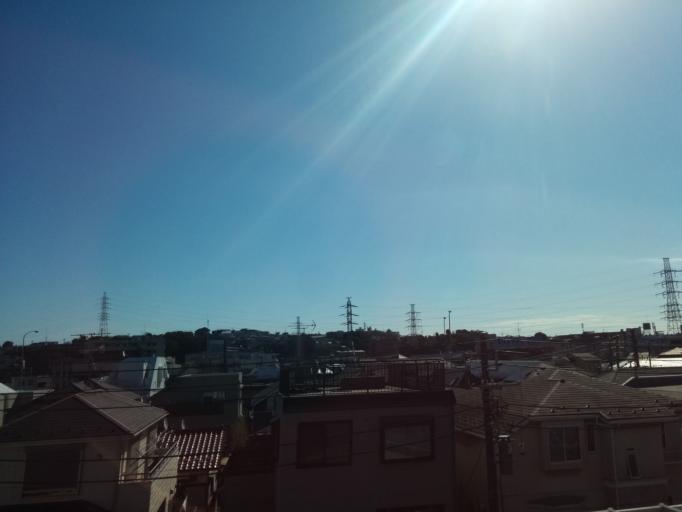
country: JP
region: Kanagawa
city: Yokohama
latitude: 35.5177
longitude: 139.6295
